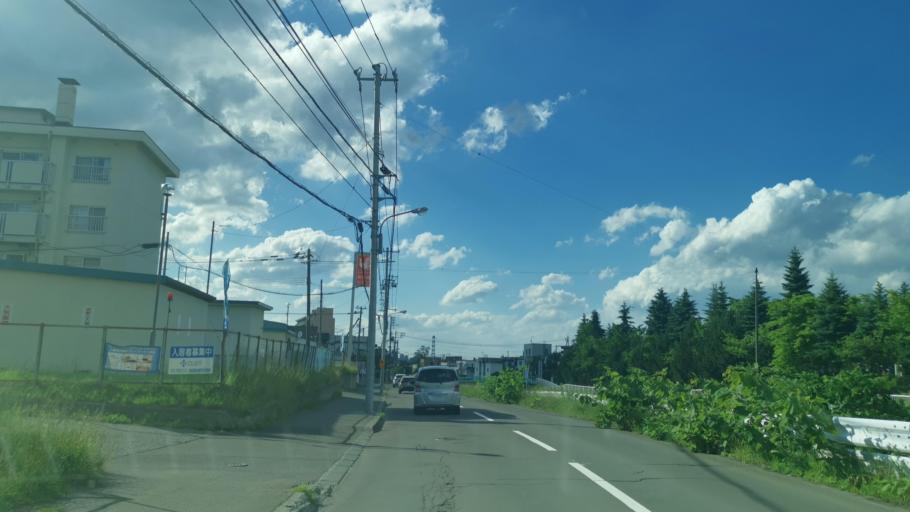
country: JP
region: Hokkaido
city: Sapporo
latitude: 43.0871
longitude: 141.2682
